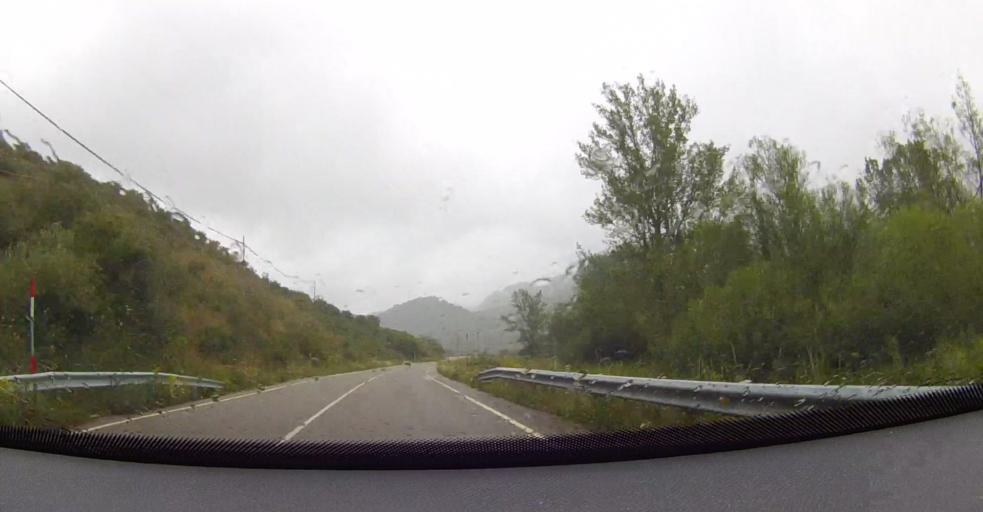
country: ES
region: Castille and Leon
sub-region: Provincia de Leon
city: Acebedo
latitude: 43.0419
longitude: -5.1103
